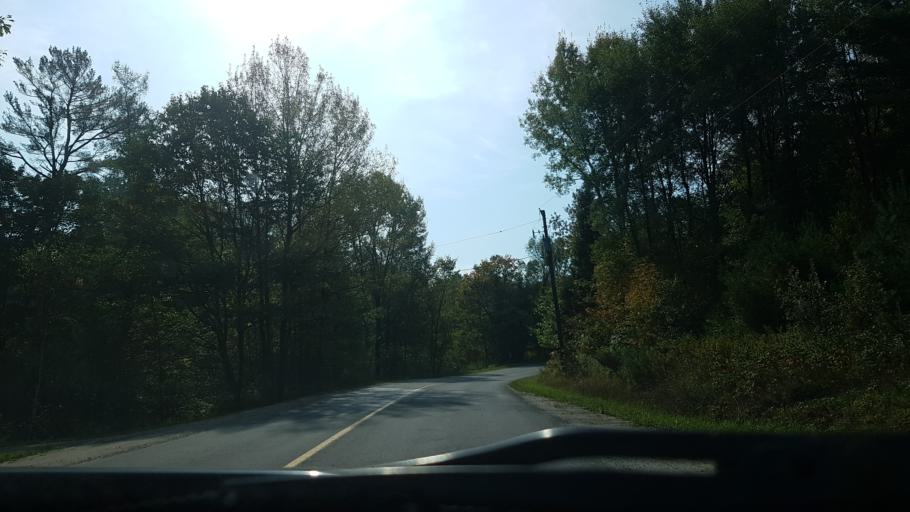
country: CA
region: Ontario
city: Gravenhurst
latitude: 44.7966
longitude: -79.2071
